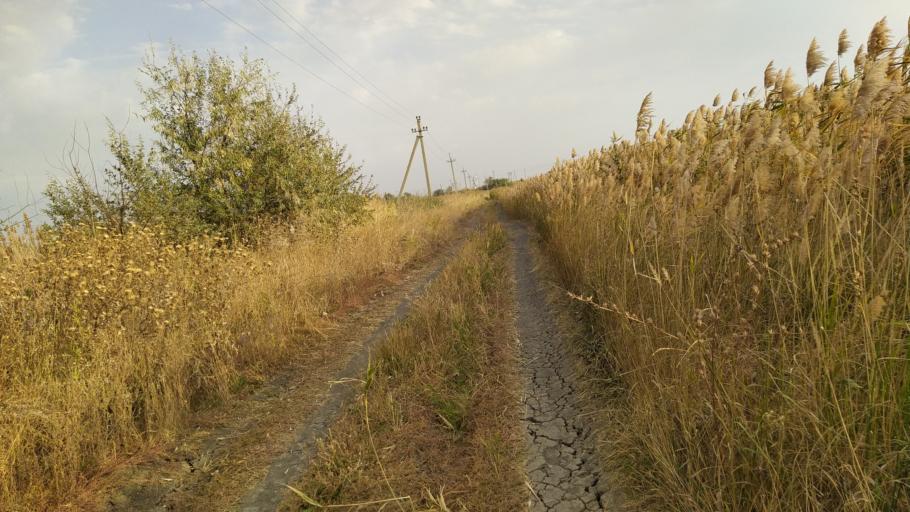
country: RU
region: Rostov
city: Kuleshovka
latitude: 47.1117
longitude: 39.6095
